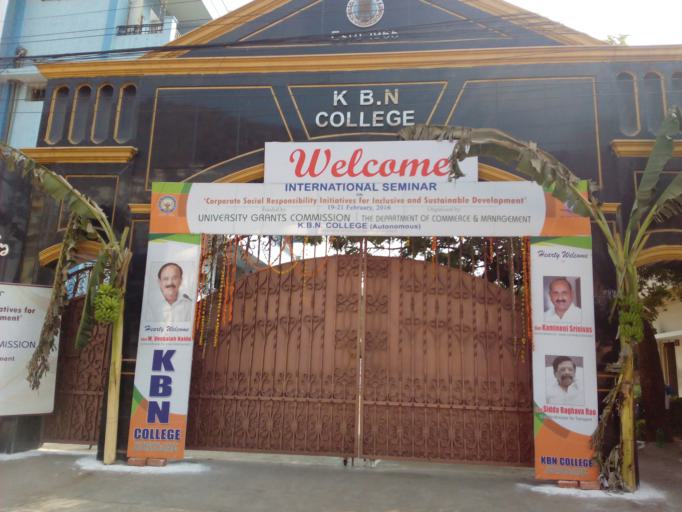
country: IN
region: Andhra Pradesh
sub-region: Krishna
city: Vijayawada
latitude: 16.5229
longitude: 80.6106
